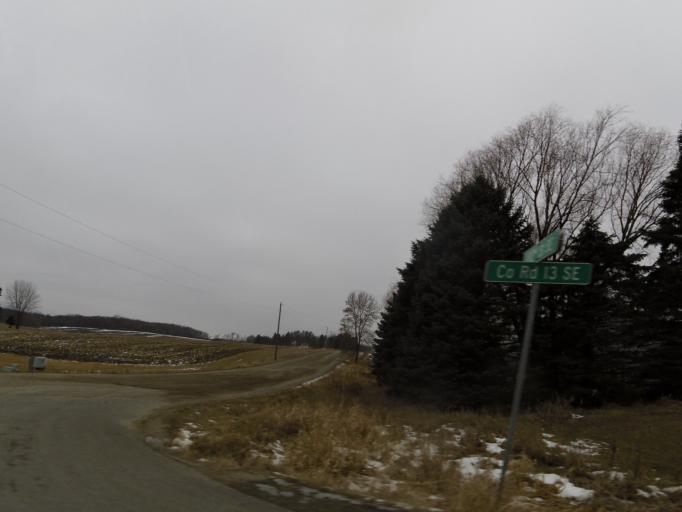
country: US
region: Minnesota
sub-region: Carver County
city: Watertown
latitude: 45.0035
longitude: -93.8488
